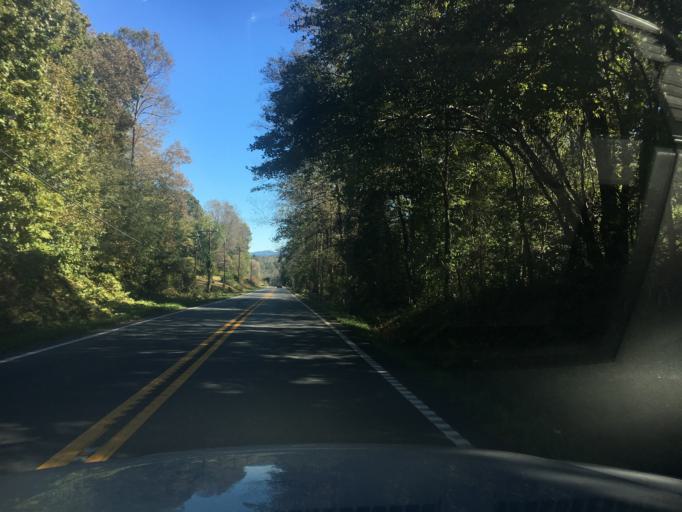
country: US
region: North Carolina
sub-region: Rutherford County
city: Rutherfordton
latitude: 35.3925
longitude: -81.9347
